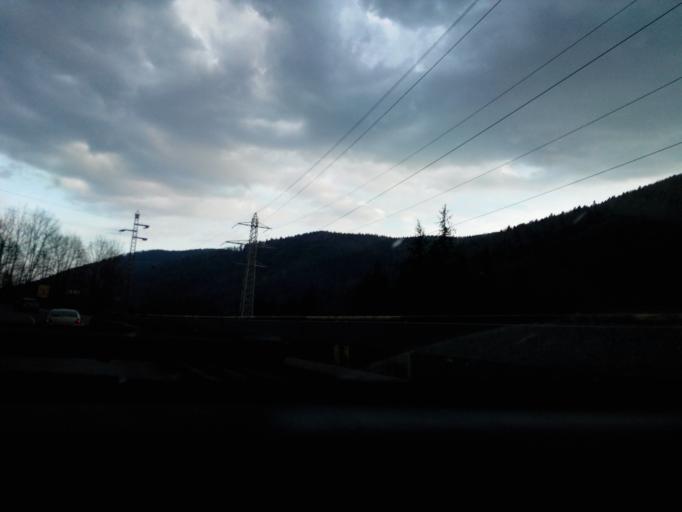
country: RO
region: Prahova
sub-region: Oras Sinaia
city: Sinaia
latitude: 45.3080
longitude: 25.5736
